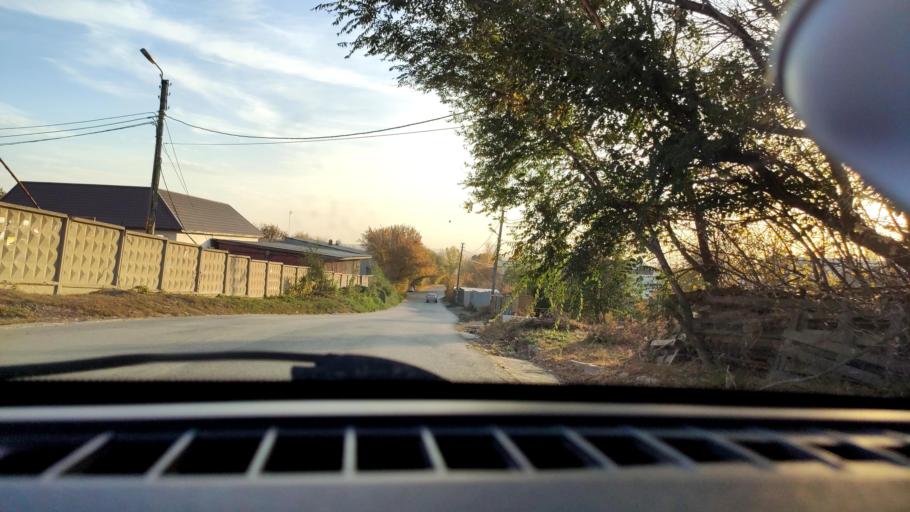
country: RU
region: Samara
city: Samara
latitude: 53.1783
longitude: 50.1560
